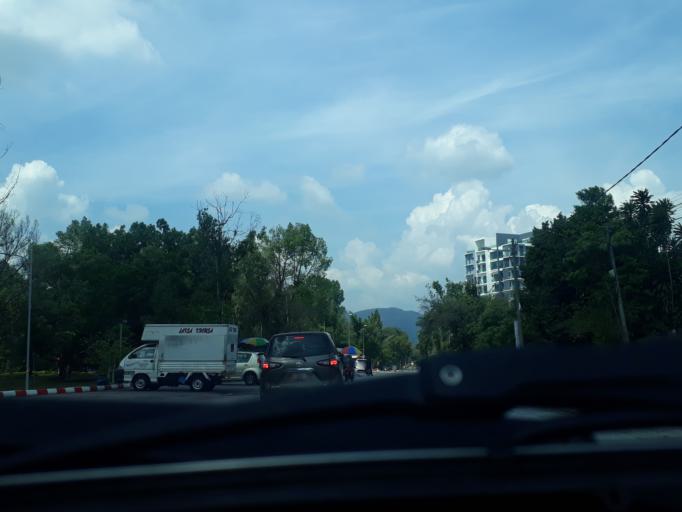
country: MY
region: Perak
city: Ipoh
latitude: 4.5951
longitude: 101.1116
